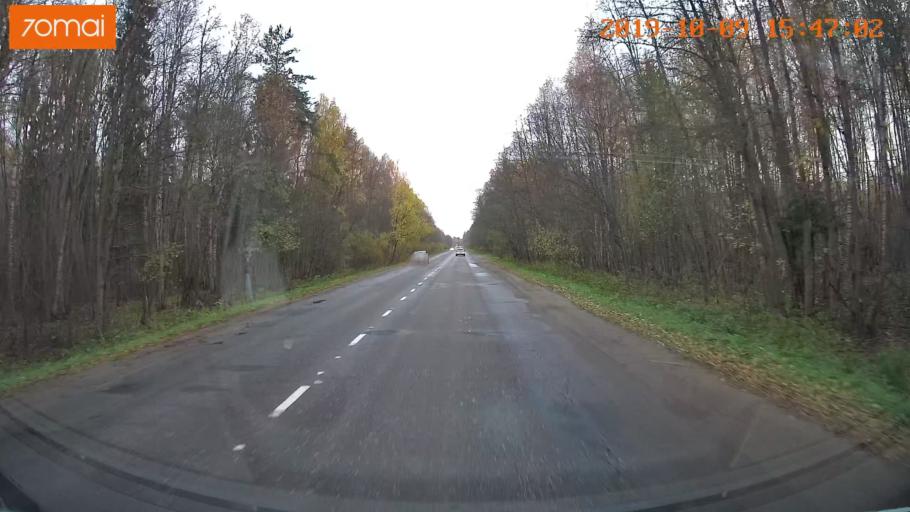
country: RU
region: Kostroma
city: Oktyabr'skiy
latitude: 57.8203
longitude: 41.0347
